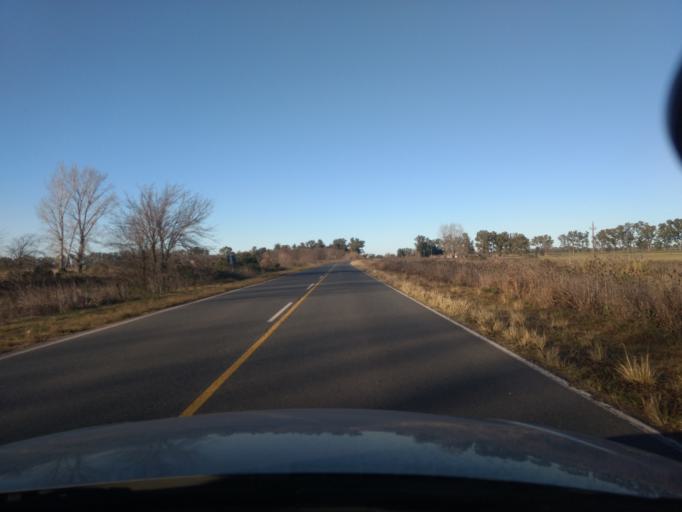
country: AR
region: Buenos Aires
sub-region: Partido de Lujan
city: Lujan
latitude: -34.6204
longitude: -59.1072
